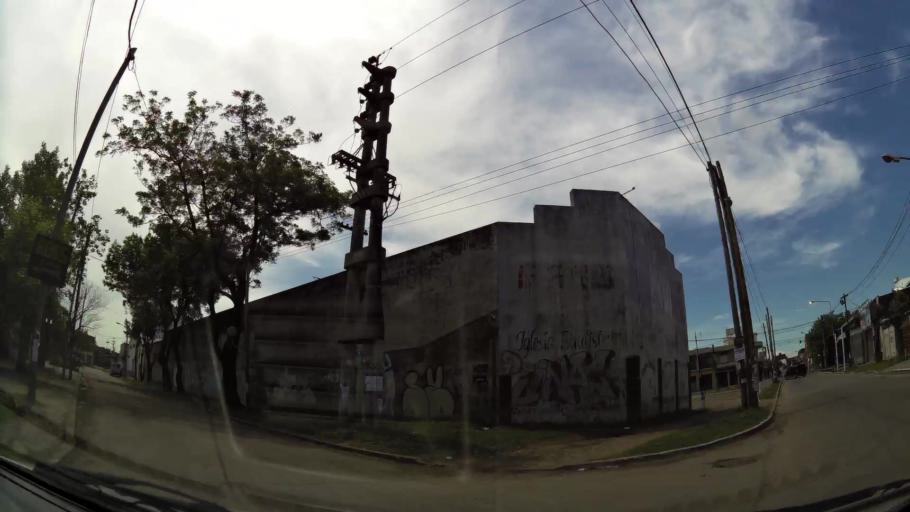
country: AR
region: Buenos Aires
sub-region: Partido de Quilmes
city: Quilmes
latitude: -34.7799
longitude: -58.2656
